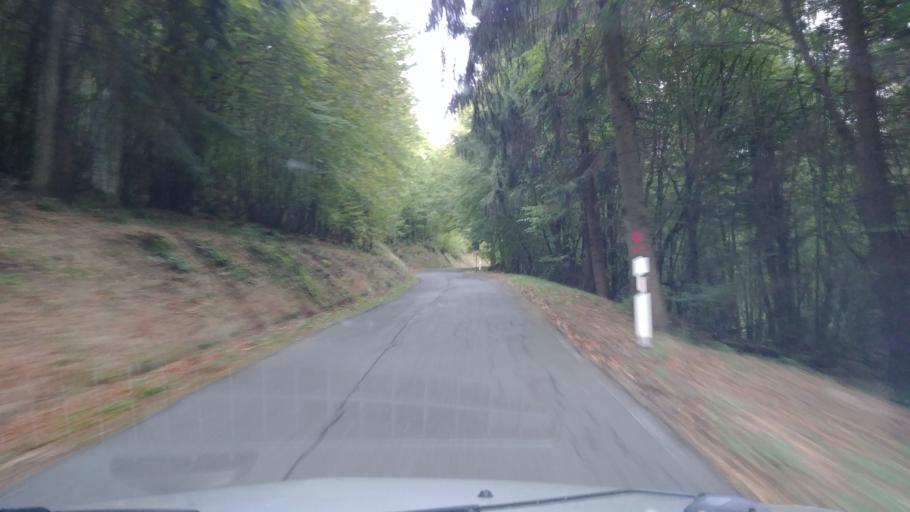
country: DE
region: Rheinland-Pfalz
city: Merschbach
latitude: 49.8137
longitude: 7.0080
